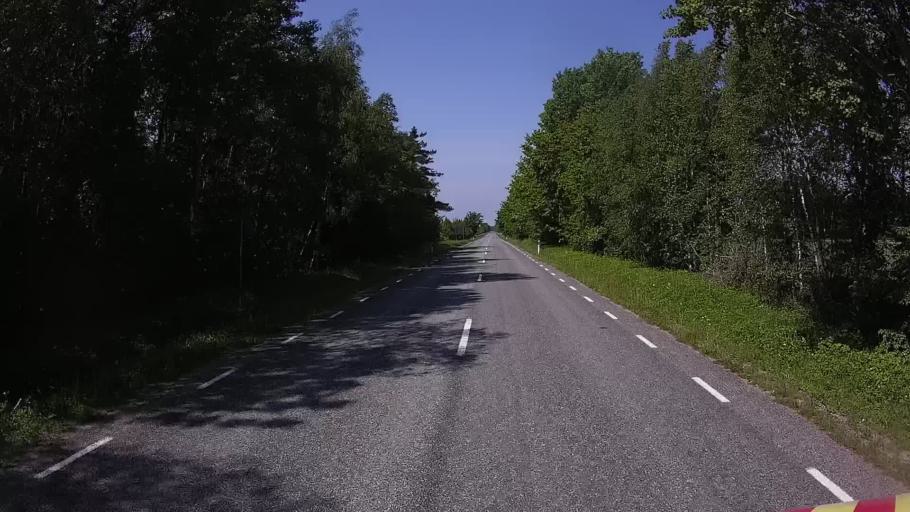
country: EE
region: Saare
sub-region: Kuressaare linn
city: Kuressaare
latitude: 58.3657
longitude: 22.0536
